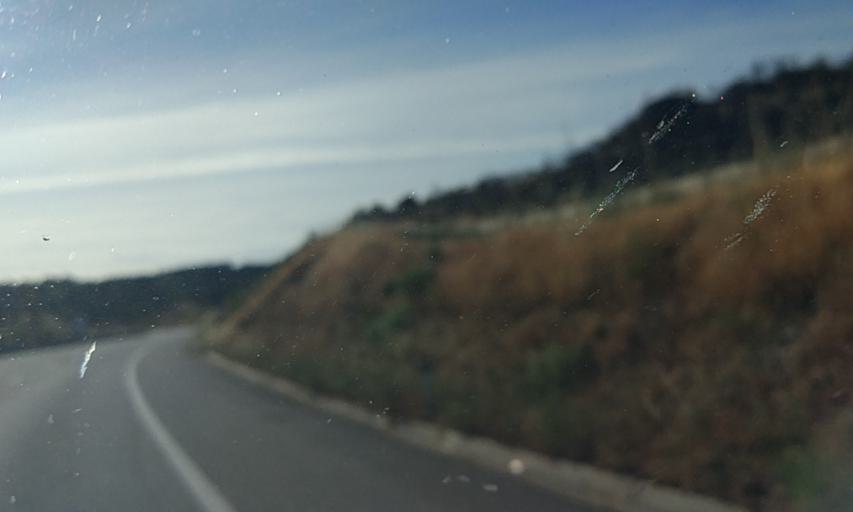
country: PT
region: Vila Real
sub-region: Murca
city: Murca
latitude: 41.4000
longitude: -7.4632
